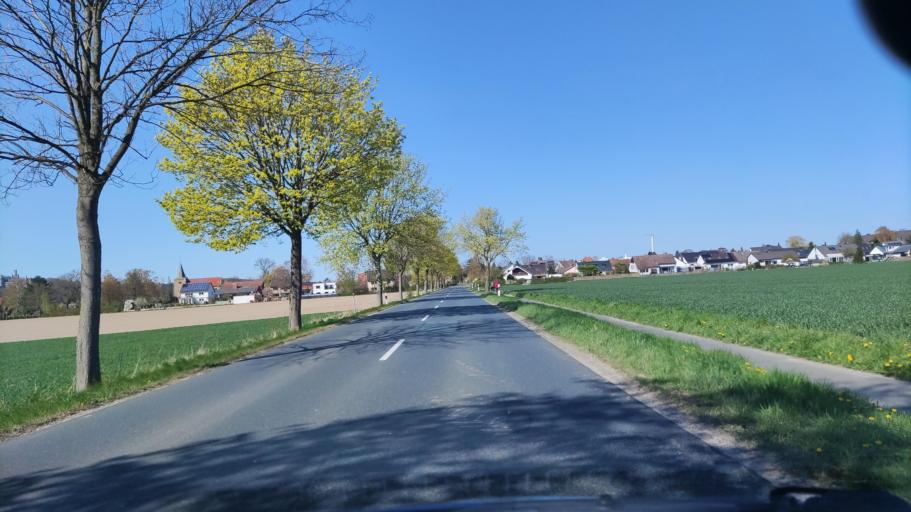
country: DE
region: Lower Saxony
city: Nordstemmen
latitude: 52.1538
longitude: 9.7773
